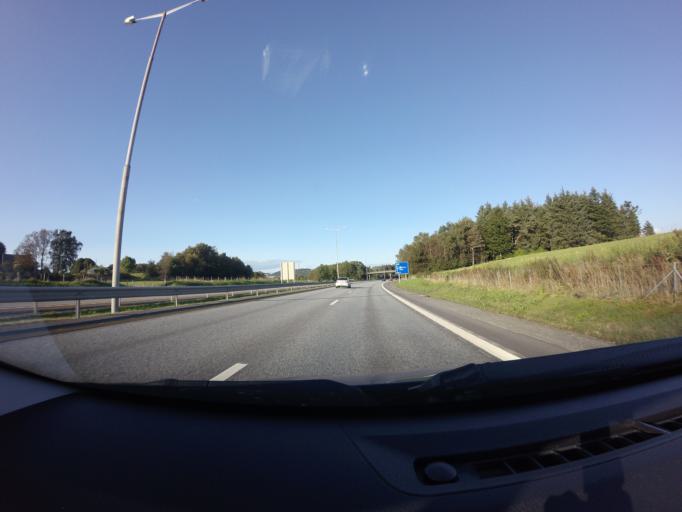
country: NO
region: Rogaland
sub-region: Sola
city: Sola
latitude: 58.9157
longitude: 5.6968
